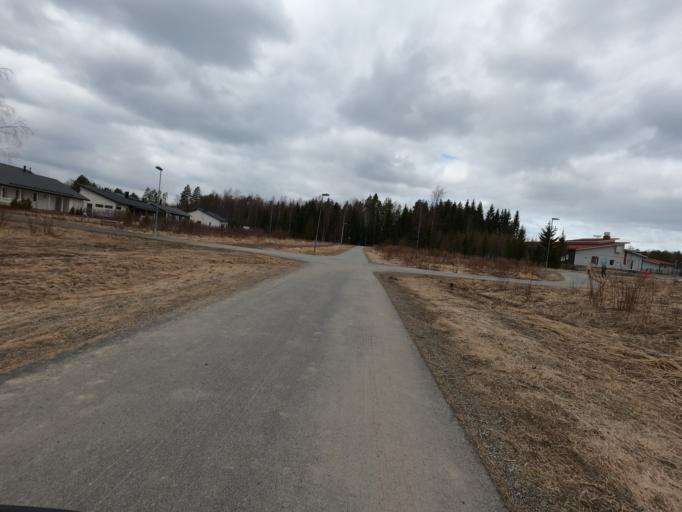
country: FI
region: North Karelia
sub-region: Joensuu
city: Joensuu
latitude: 62.5685
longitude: 29.8154
